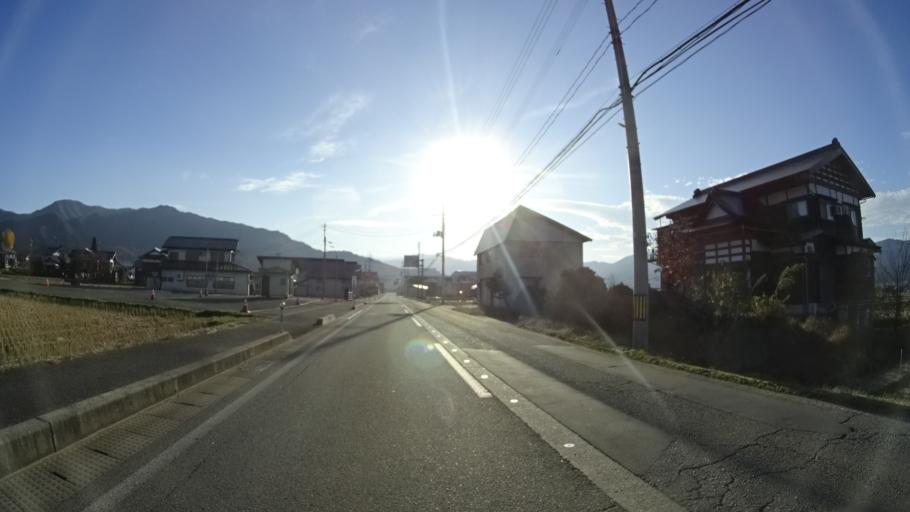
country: JP
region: Niigata
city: Shiozawa
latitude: 37.0176
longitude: 138.8591
